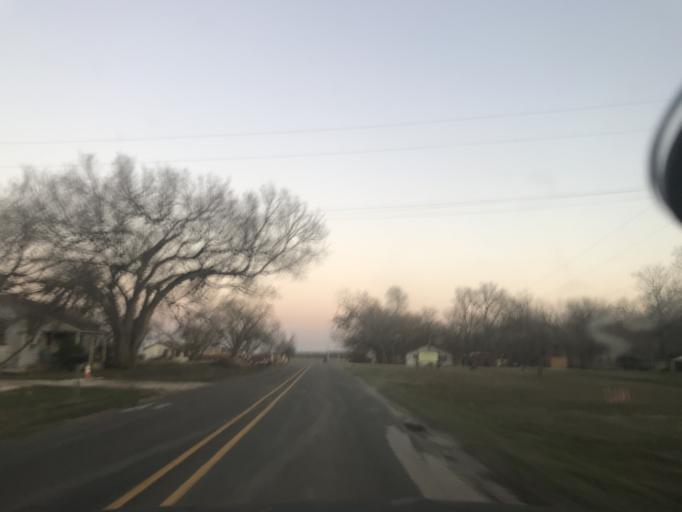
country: US
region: Texas
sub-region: Williamson County
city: Hutto
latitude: 30.5001
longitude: -97.5105
